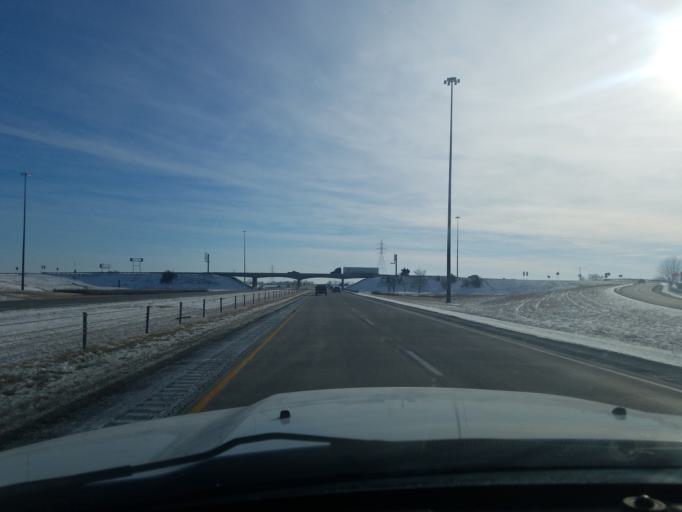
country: US
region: Indiana
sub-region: Grant County
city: Upland
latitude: 40.4251
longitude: -85.5497
